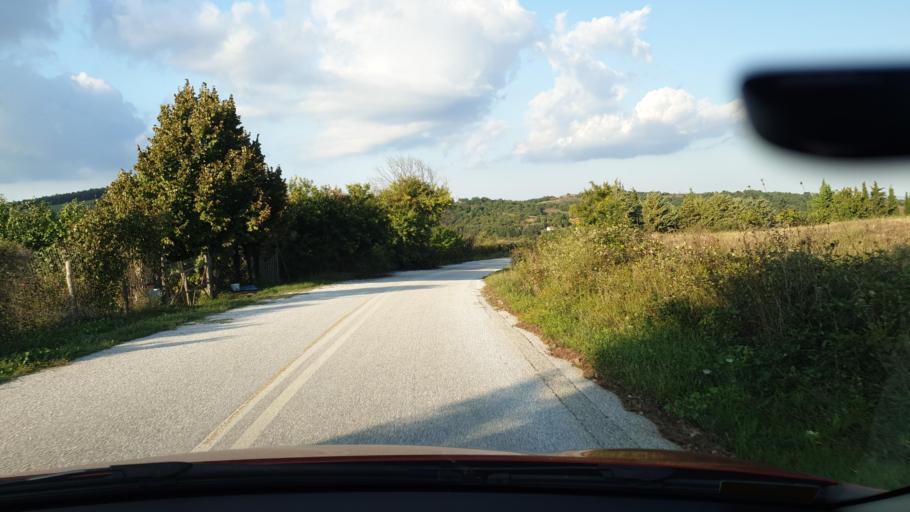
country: GR
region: Central Macedonia
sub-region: Nomos Chalkidikis
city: Galatista
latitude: 40.5198
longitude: 23.2754
